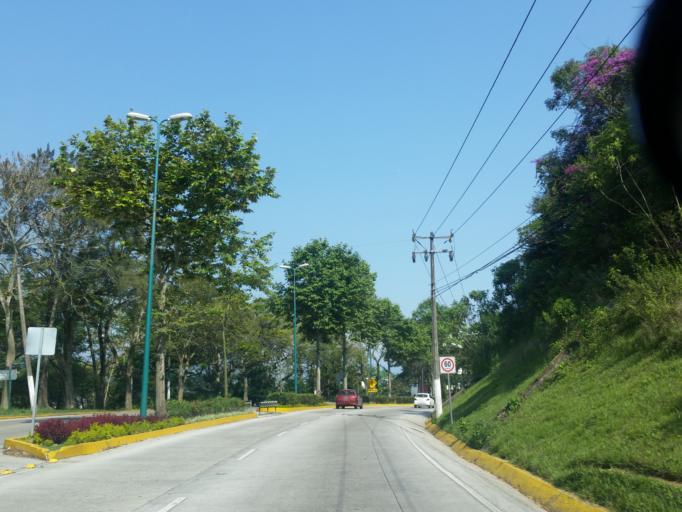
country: MX
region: Veracruz
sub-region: Xalapa
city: Xalapa de Enriquez
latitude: 19.5192
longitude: -96.9037
